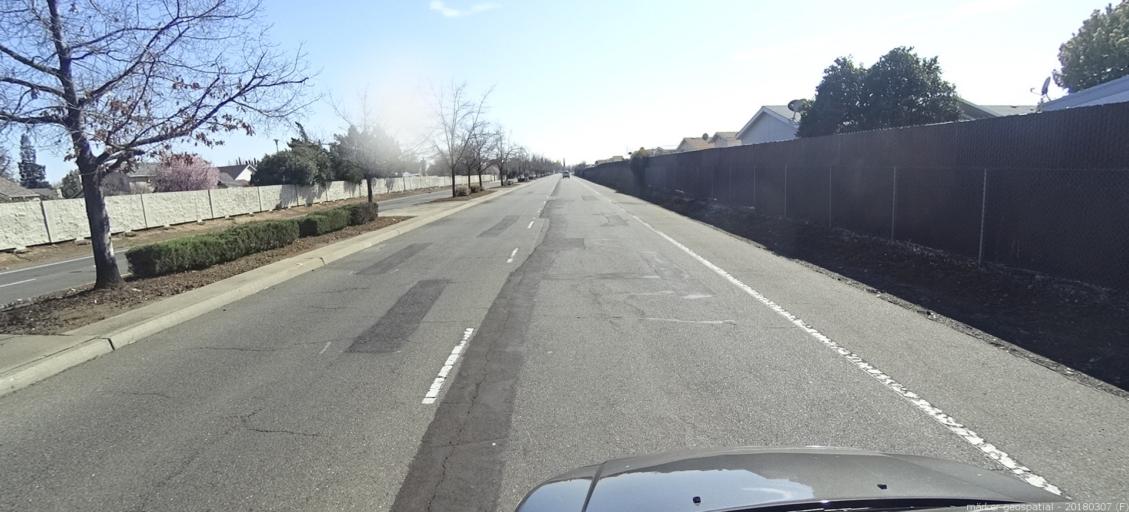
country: US
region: California
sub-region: Sacramento County
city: Florin
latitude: 38.5080
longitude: -121.4276
